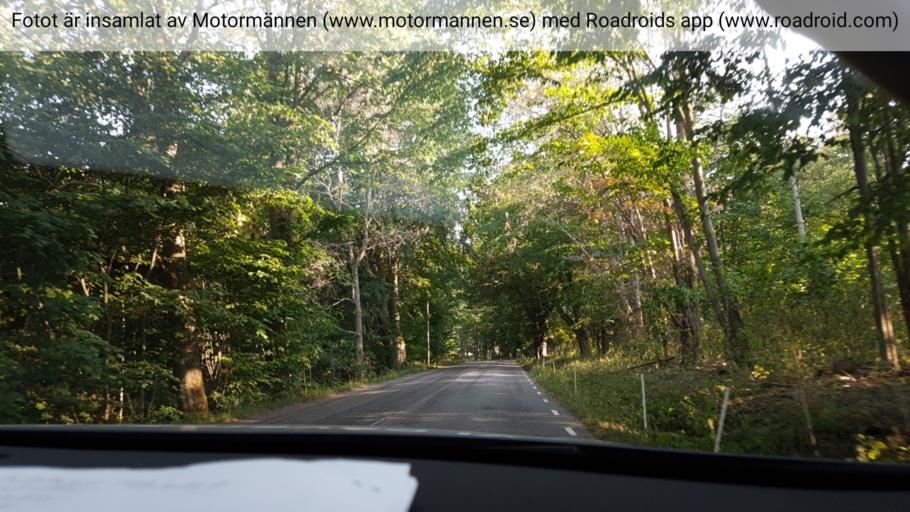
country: SE
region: Vaestra Goetaland
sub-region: Skovde Kommun
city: Stopen
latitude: 58.4708
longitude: 13.8387
